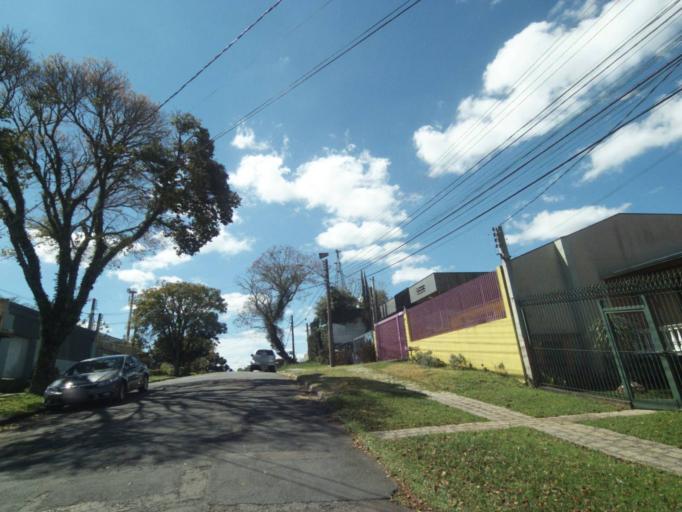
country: BR
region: Parana
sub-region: Curitiba
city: Curitiba
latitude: -25.4007
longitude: -49.2732
